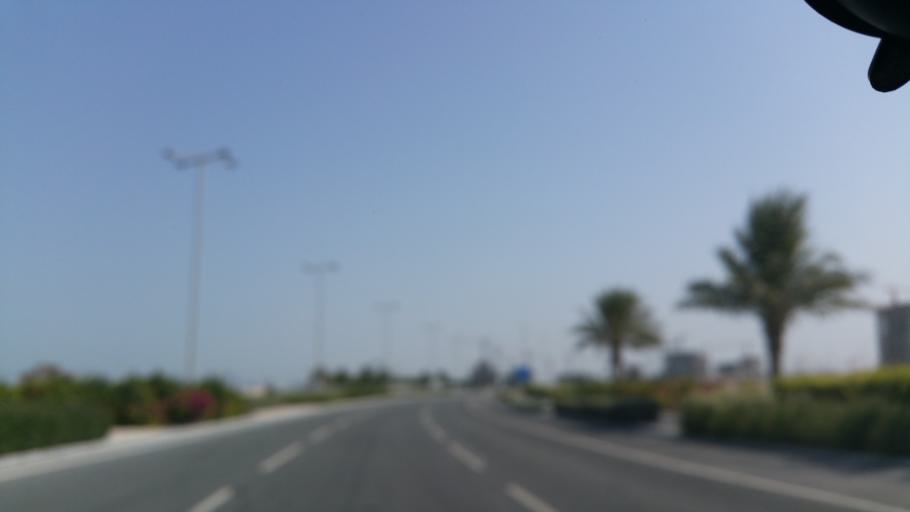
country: QA
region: Baladiyat Umm Salal
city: Umm Salal Muhammad
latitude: 25.4363
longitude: 51.5149
